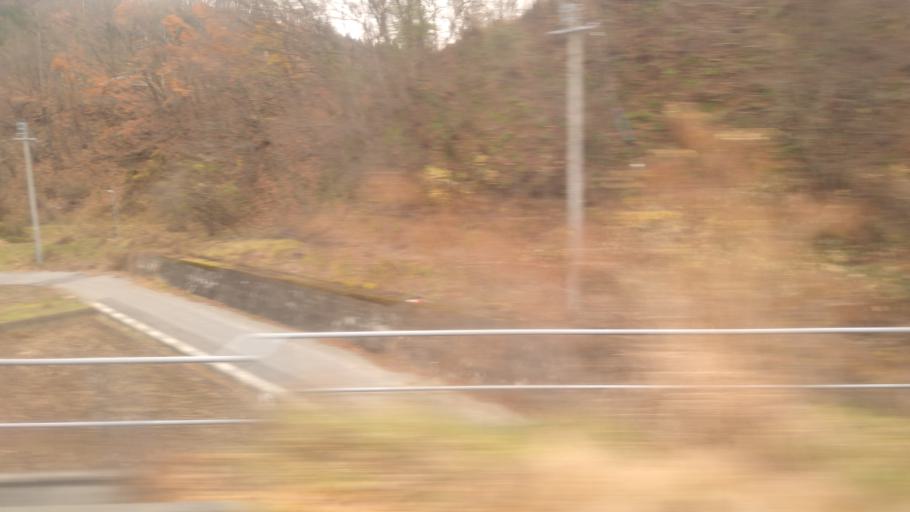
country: JP
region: Nagano
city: Hotaka
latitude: 36.3588
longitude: 137.9348
